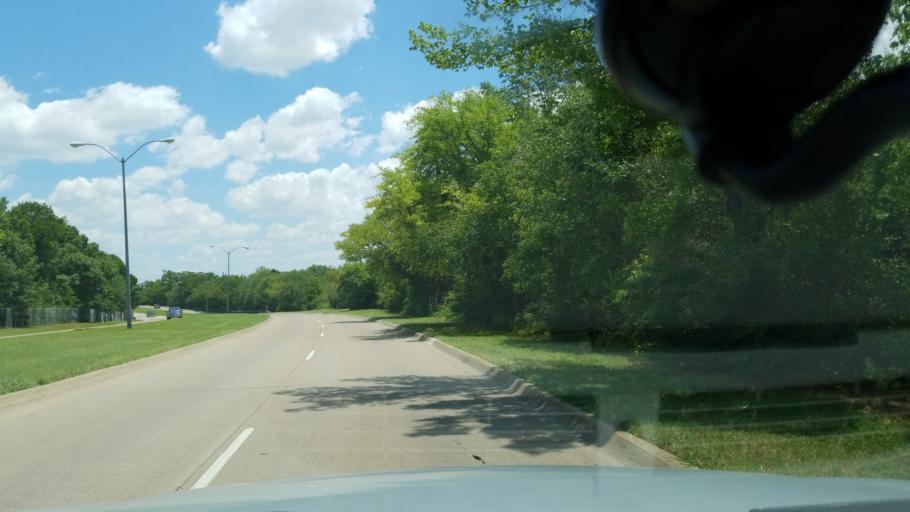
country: US
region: Texas
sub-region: Dallas County
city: Duncanville
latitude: 32.6715
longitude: -96.8716
